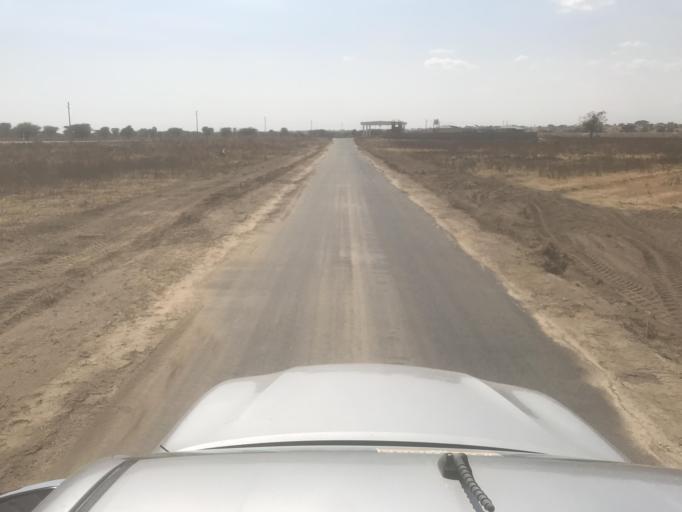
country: ET
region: Oromiya
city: Ziway
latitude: 8.1461
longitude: 38.7990
